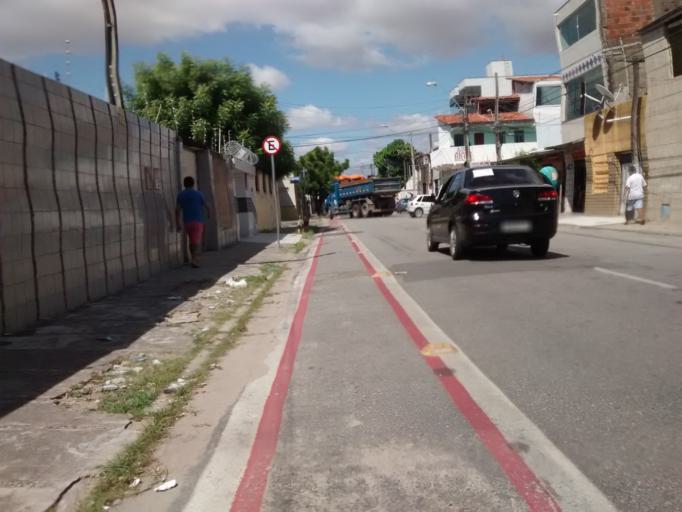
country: BR
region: Ceara
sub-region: Fortaleza
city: Fortaleza
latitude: -3.7267
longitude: -38.5515
